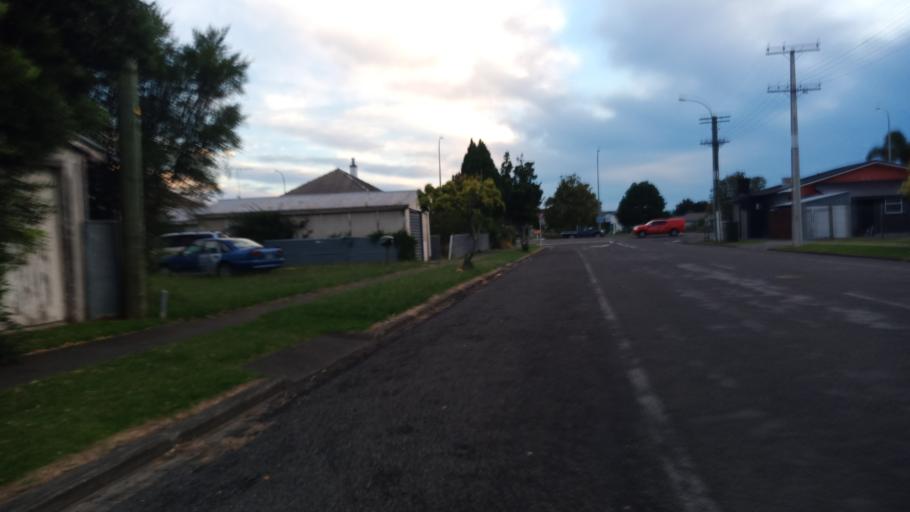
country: NZ
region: Gisborne
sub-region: Gisborne District
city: Gisborne
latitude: -38.6520
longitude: 178.0012
